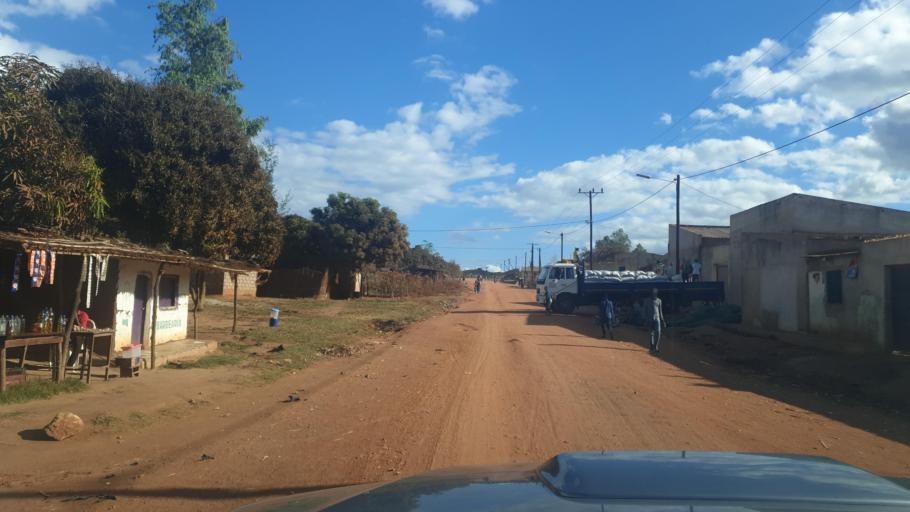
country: MZ
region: Nampula
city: Nampula
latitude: -15.0998
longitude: 39.2229
